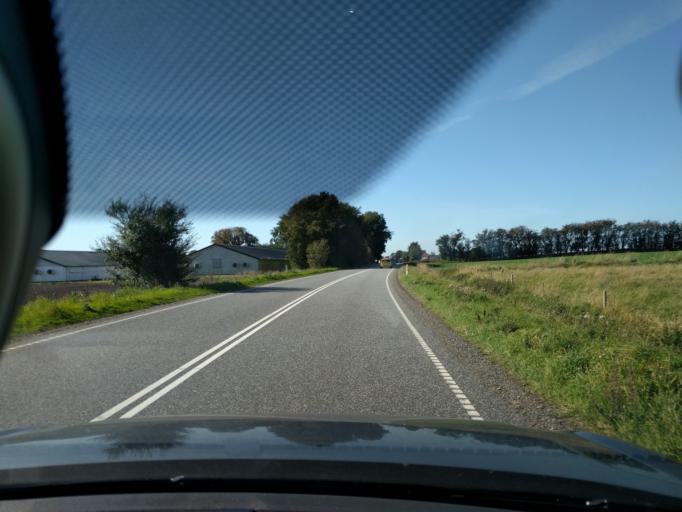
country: DK
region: North Denmark
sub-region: Mariagerfjord Kommune
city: Hobro
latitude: 56.6727
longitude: 9.6876
